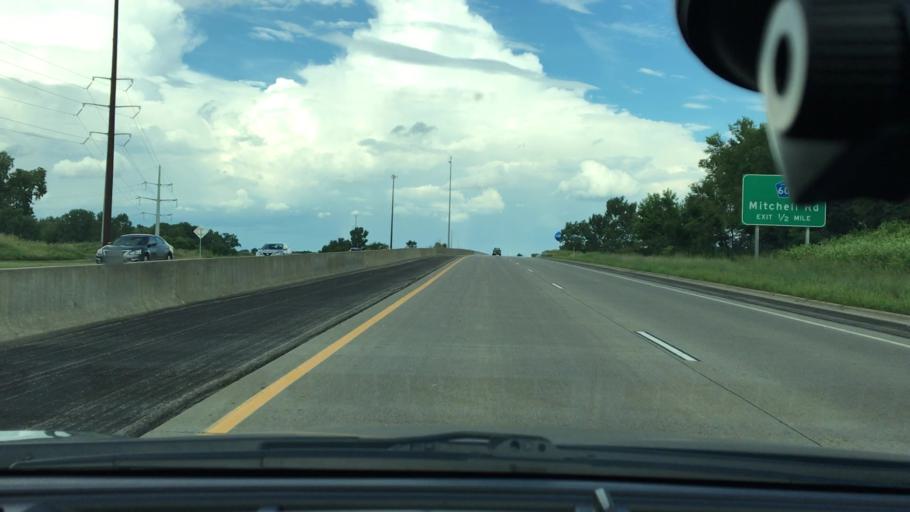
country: US
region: Minnesota
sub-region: Hennepin County
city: Eden Prairie
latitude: 44.8614
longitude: -93.4774
